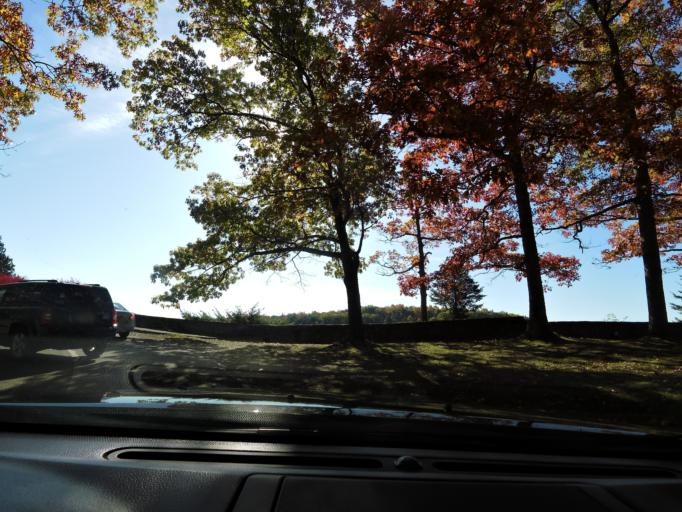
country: US
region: New York
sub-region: Wyoming County
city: Castile
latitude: 42.6074
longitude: -78.0243
